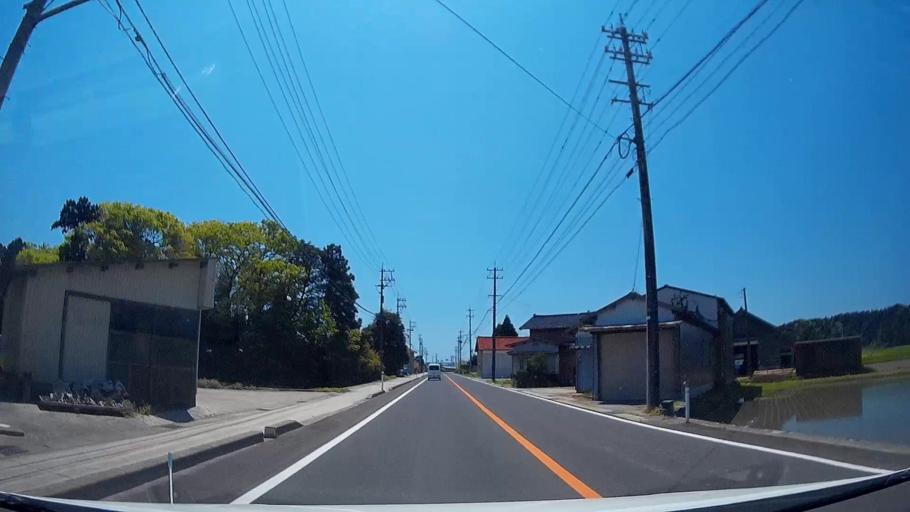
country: JP
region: Ishikawa
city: Nanao
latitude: 37.4478
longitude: 137.2836
